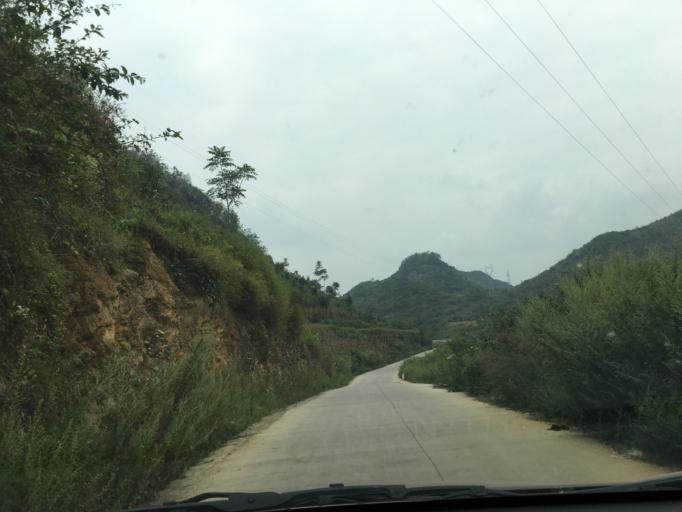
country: CN
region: Guangxi Zhuangzu Zizhiqu
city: Xinzhou
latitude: 25.5377
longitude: 105.6017
